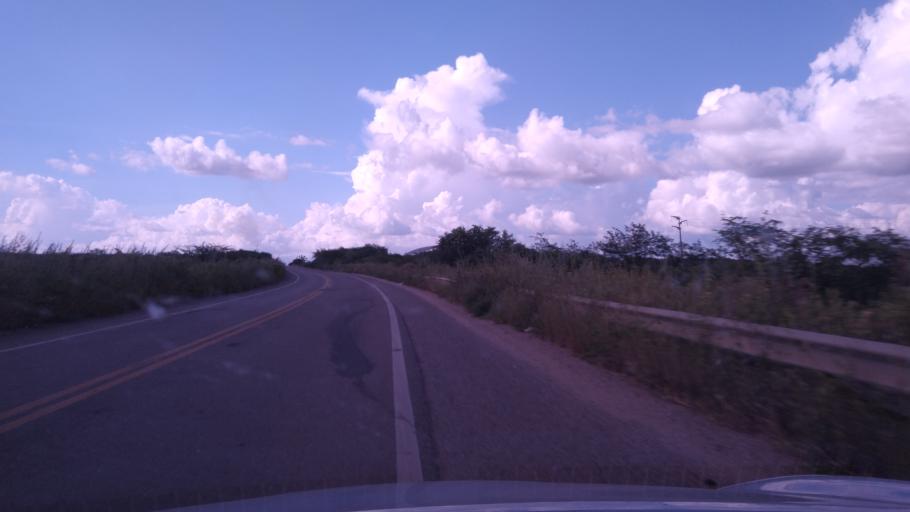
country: BR
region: Ceara
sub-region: Caninde
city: Caninde
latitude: -4.3943
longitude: -39.3145
